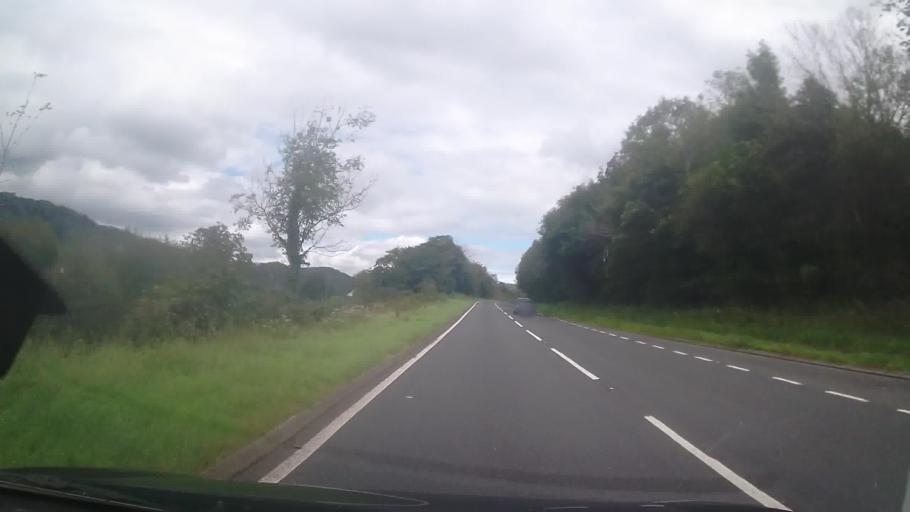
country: GB
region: Wales
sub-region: Sir Powys
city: Machynlleth
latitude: 52.5833
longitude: -3.8743
